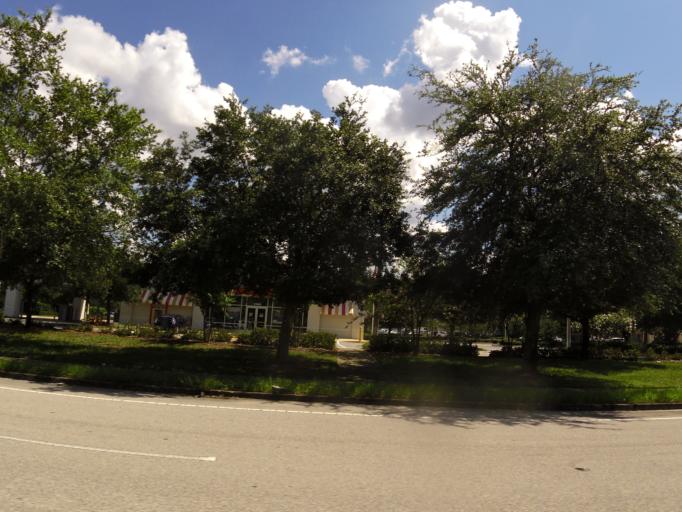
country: US
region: Florida
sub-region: Saint Johns County
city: Fruit Cove
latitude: 30.1423
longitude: -81.5489
